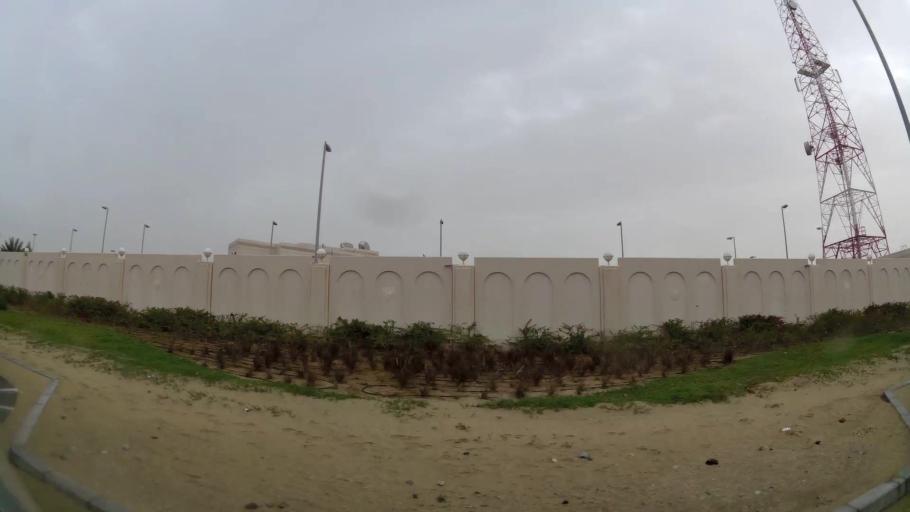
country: AE
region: Abu Dhabi
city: Abu Dhabi
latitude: 24.4334
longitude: 54.5799
